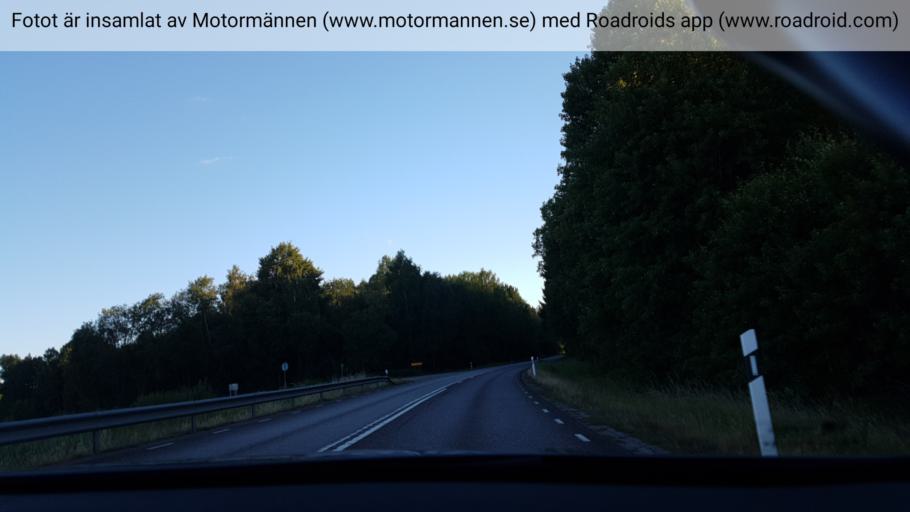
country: SE
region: Vaestra Goetaland
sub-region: Karlsborgs Kommun
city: Karlsborg
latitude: 58.4994
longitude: 14.4607
